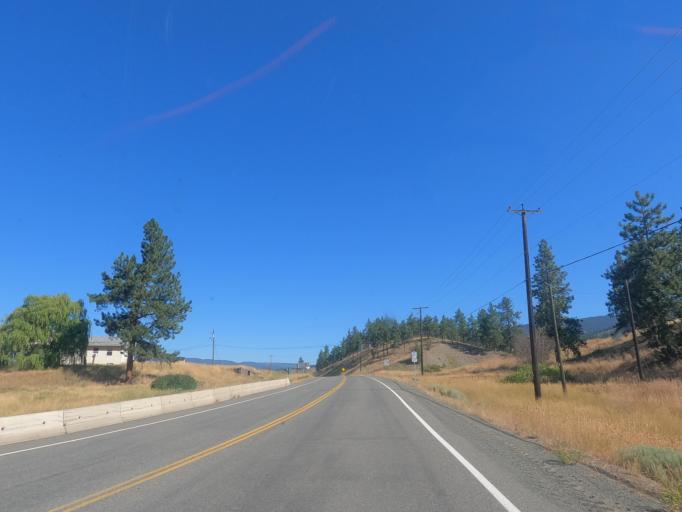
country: CA
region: British Columbia
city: Merritt
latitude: 50.1375
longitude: -120.8376
